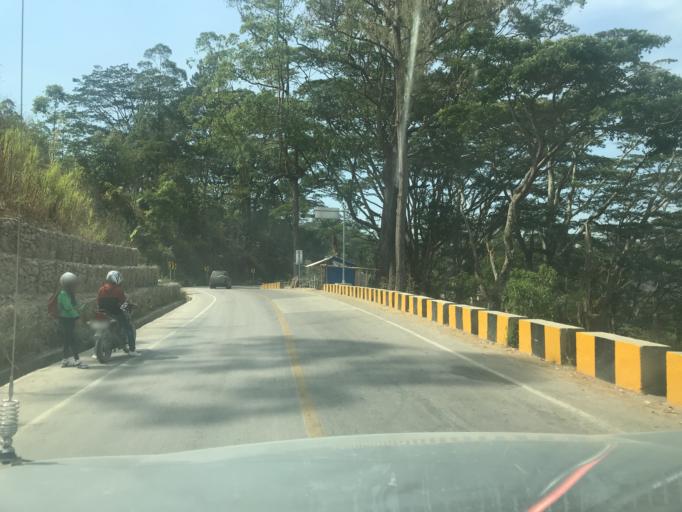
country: TL
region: Aileu
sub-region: Aileu Villa
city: Aileu
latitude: -8.6770
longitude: 125.5507
